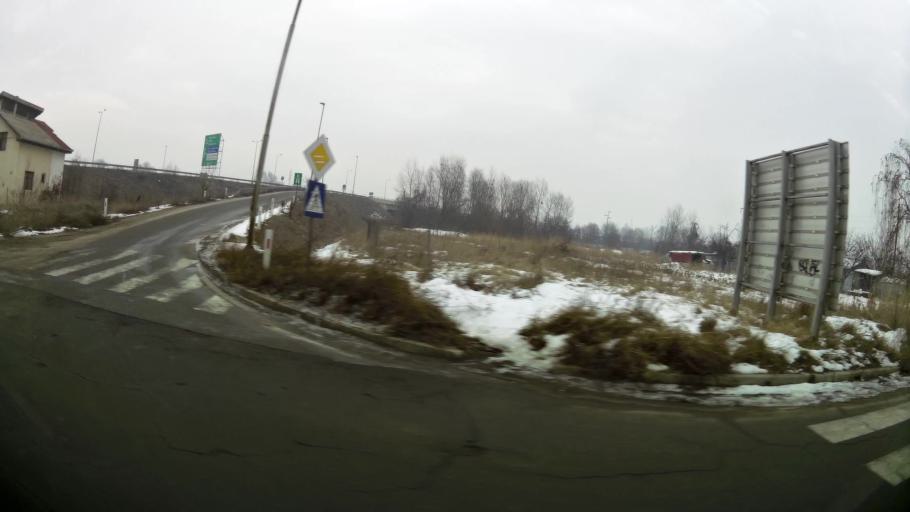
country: MK
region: Cucer-Sandevo
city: Chucher - Sandevo
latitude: 42.0524
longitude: 21.3646
